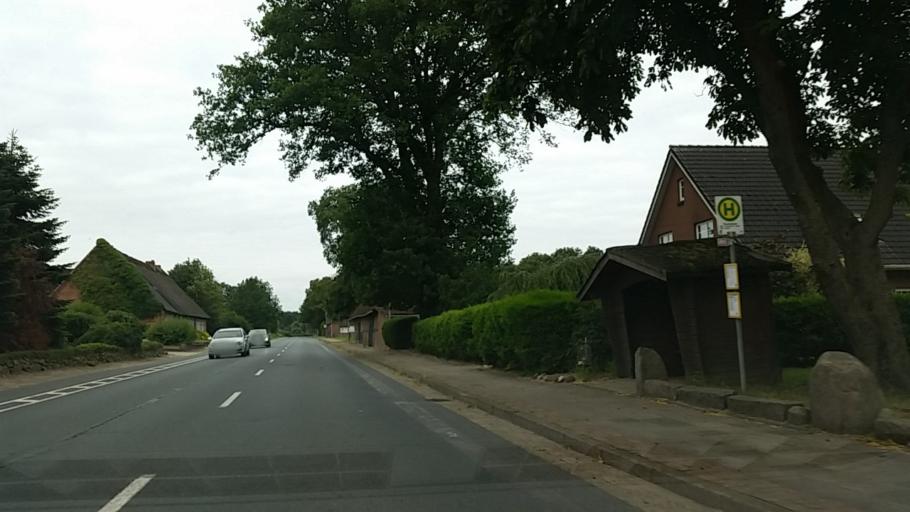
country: DE
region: Lower Saxony
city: Beverstedt
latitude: 53.4245
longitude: 8.8976
